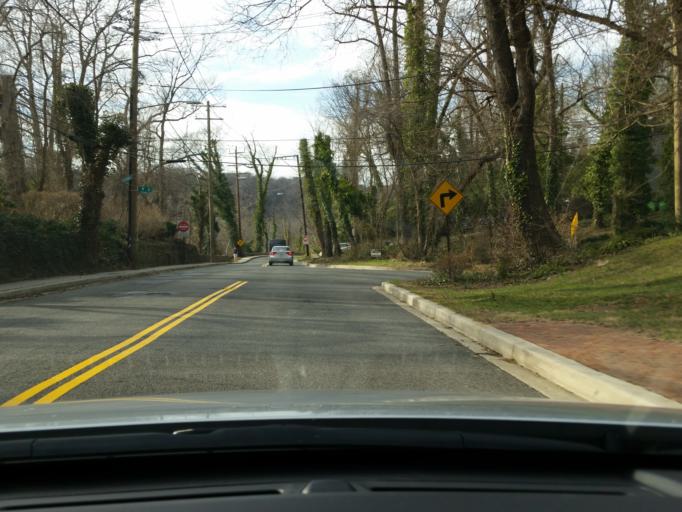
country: US
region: Maryland
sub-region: Montgomery County
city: Brookmont
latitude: 38.9167
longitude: -77.0982
